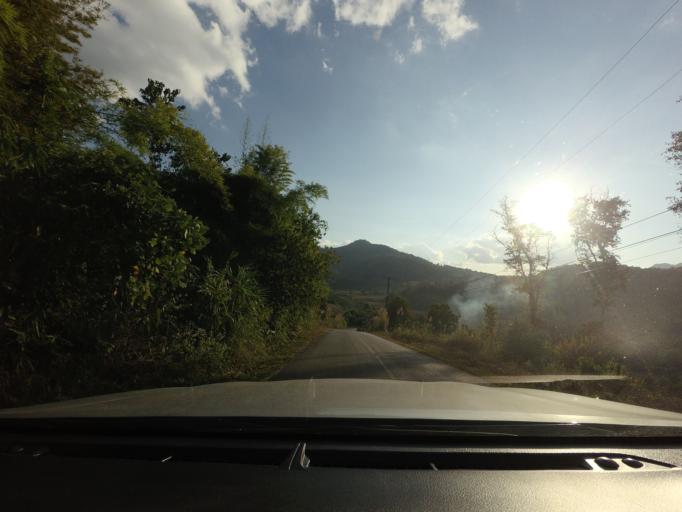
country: TH
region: Chiang Mai
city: Phrao
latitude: 19.4970
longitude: 99.1672
